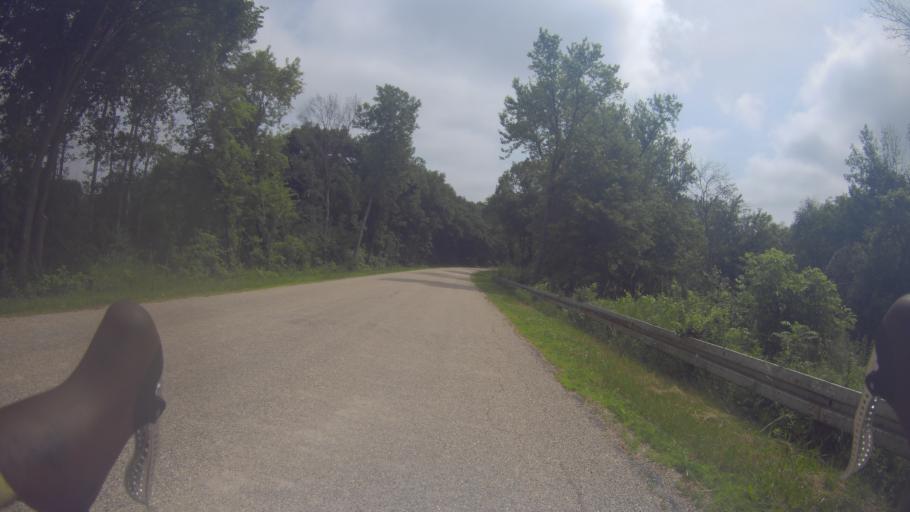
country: US
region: Wisconsin
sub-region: Jefferson County
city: Cambridge
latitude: 42.9222
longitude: -89.0254
